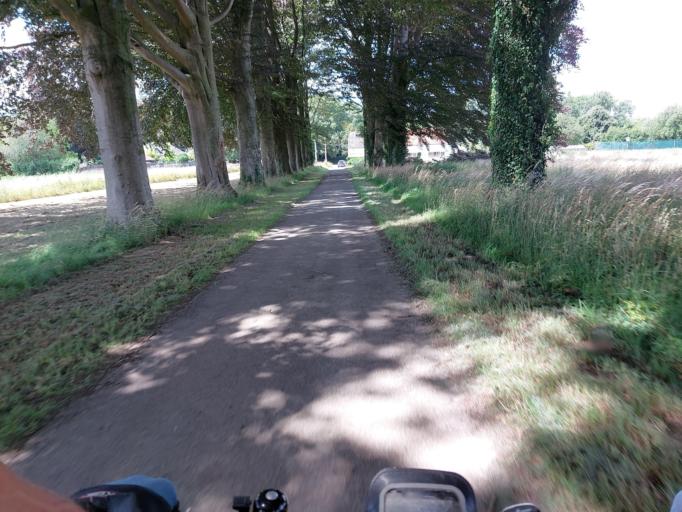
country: BE
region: Wallonia
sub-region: Province du Hainaut
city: Silly
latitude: 50.5974
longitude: 3.9433
